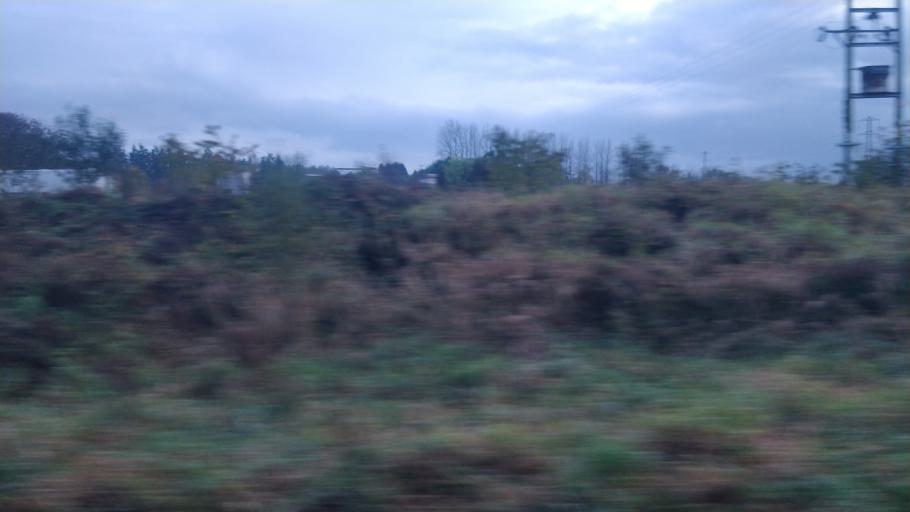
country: GB
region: England
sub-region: Lancashire
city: Parbold
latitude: 53.5956
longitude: -2.7942
